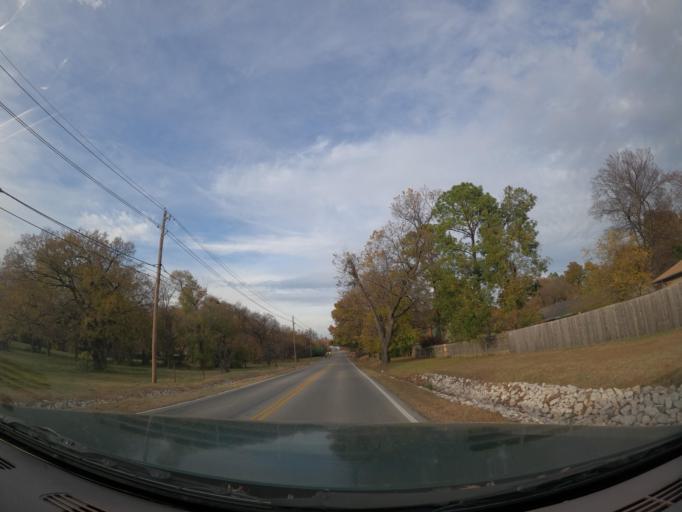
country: US
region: Oklahoma
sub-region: Tulsa County
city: Jenks
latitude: 36.0398
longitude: -95.9400
